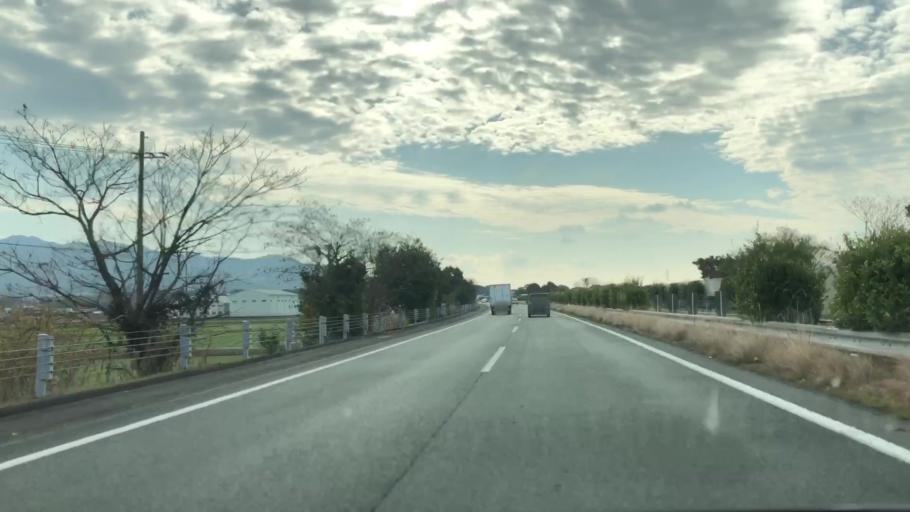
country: JP
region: Fukuoka
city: Setakamachi-takayanagi
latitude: 33.1909
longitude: 130.5204
